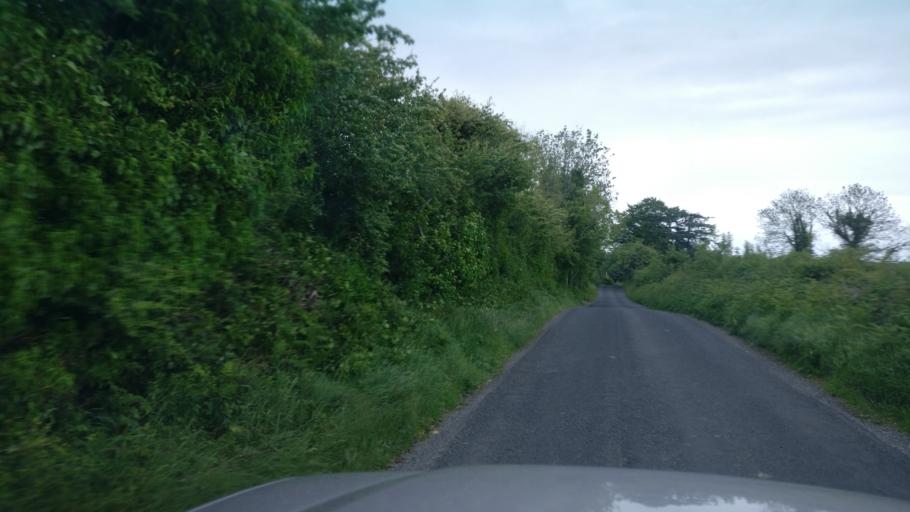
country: IE
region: Connaught
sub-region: County Galway
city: Loughrea
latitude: 53.1247
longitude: -8.4259
